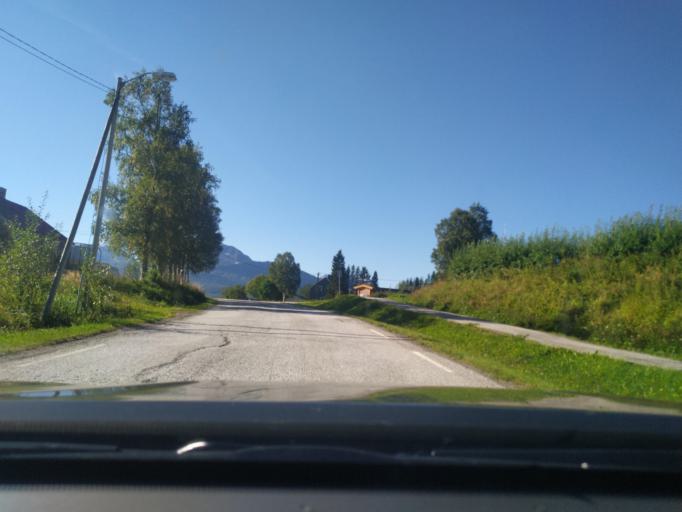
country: NO
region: Troms
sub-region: Salangen
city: Sjovegan
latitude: 68.9371
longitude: 17.7174
